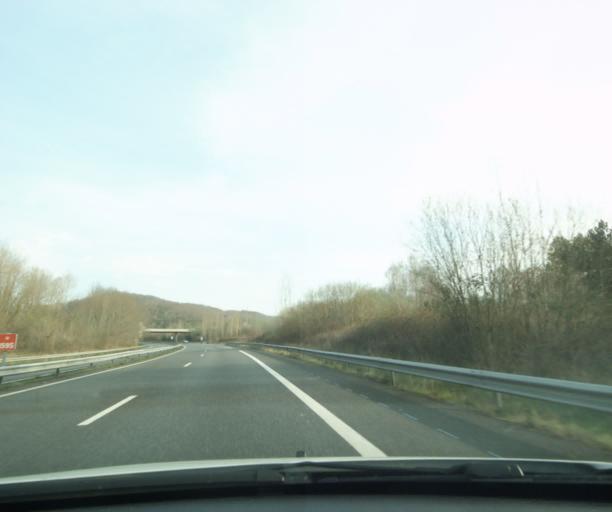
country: FR
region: Midi-Pyrenees
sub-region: Departement des Hautes-Pyrenees
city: Tournay
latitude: 43.1659
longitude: 0.2528
